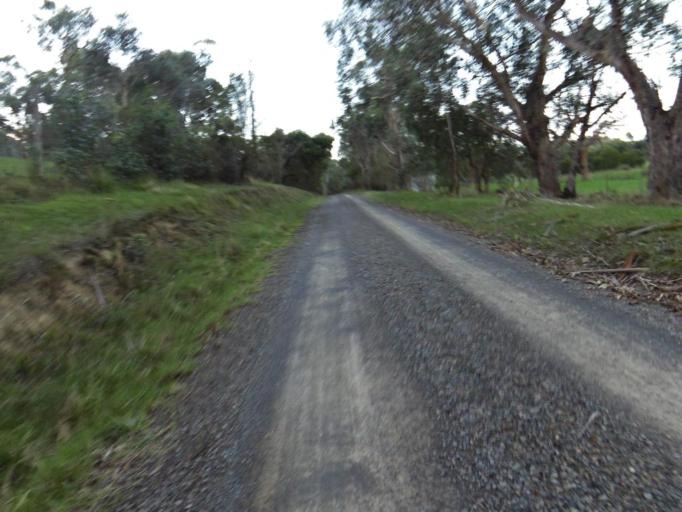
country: AU
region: Victoria
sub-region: Manningham
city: Warrandyte
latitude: -37.7416
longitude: 145.2376
